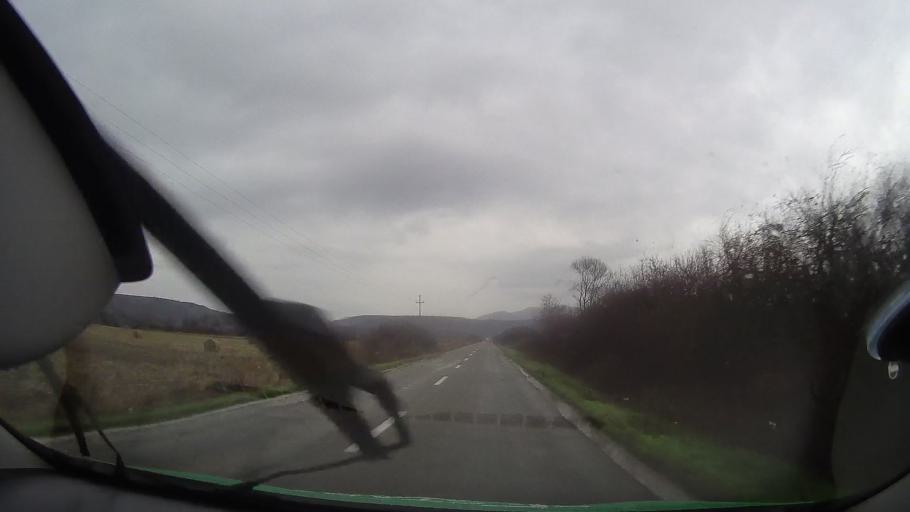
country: RO
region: Bihor
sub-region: Comuna Soimi
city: Soimi
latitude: 46.6930
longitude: 22.0978
